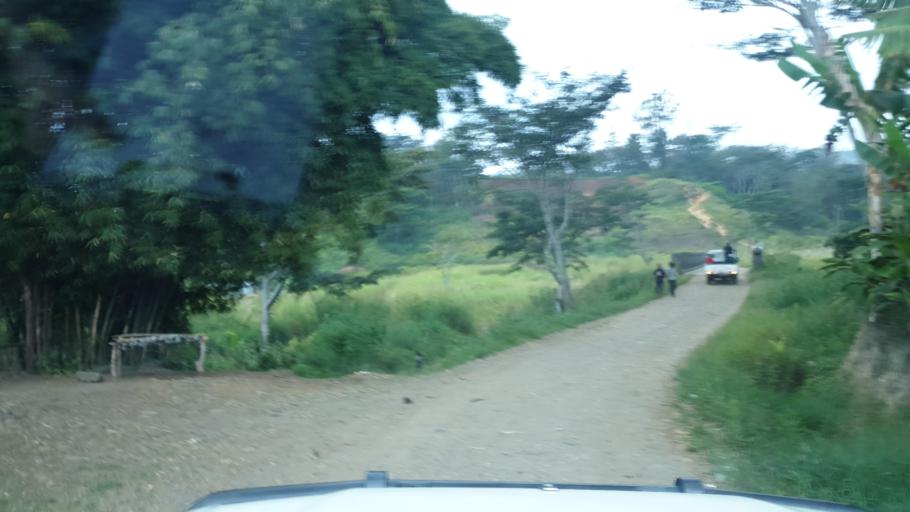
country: PG
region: Eastern Highlands
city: Goroka
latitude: -5.9859
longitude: 145.2827
